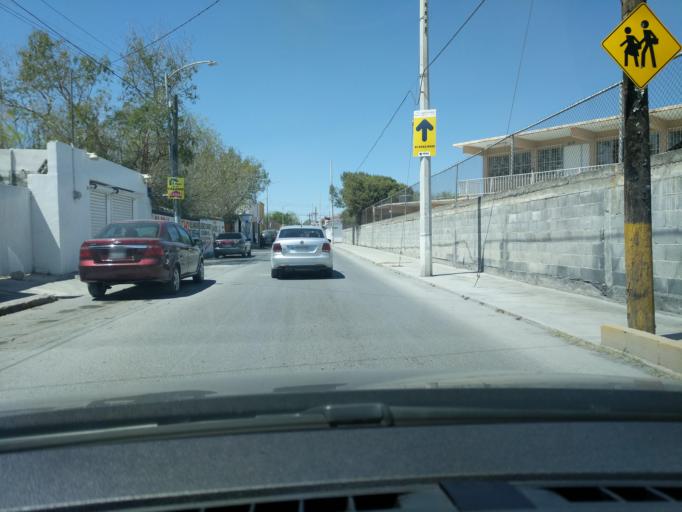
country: MX
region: Nuevo Leon
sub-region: Salinas Victoria
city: Las Torres
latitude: 25.9631
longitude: -100.2934
